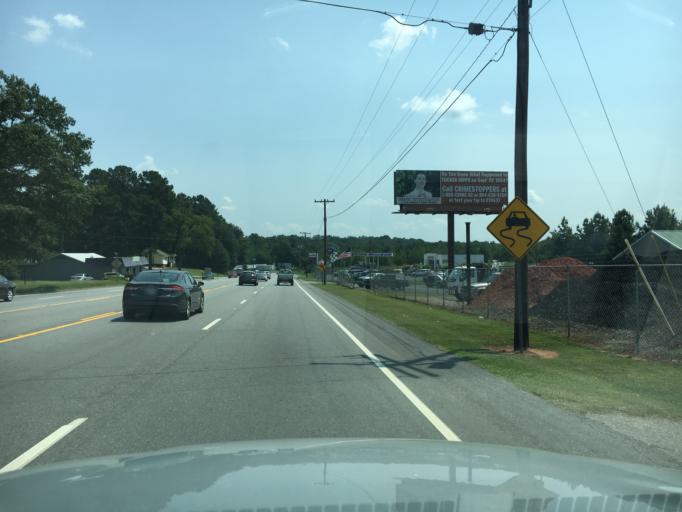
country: US
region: South Carolina
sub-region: Anderson County
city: Pendleton
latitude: 34.6093
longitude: -82.7675
